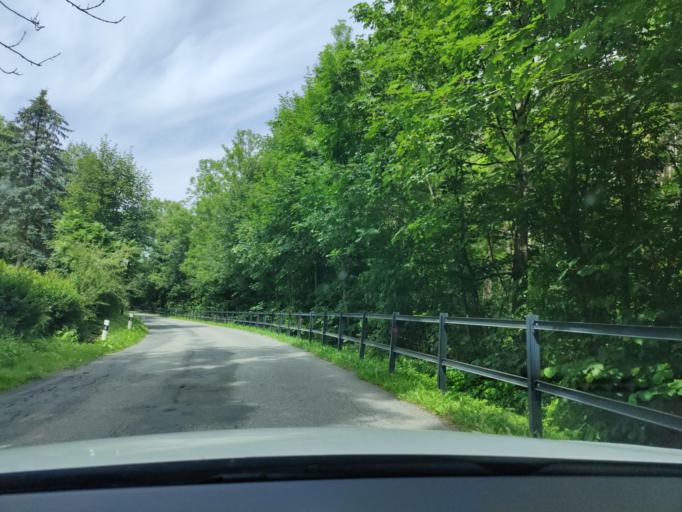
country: CZ
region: Olomoucky
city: Zlate Hory
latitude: 50.2258
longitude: 17.3455
